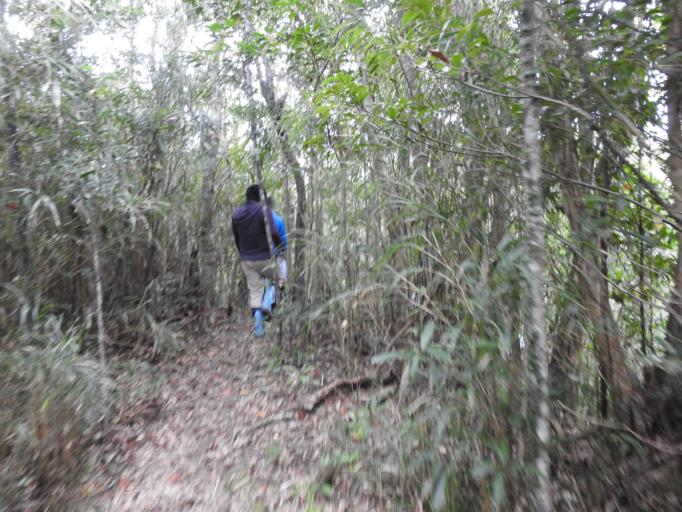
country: JP
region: Okinawa
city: Nago
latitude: 26.7145
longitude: 128.2694
